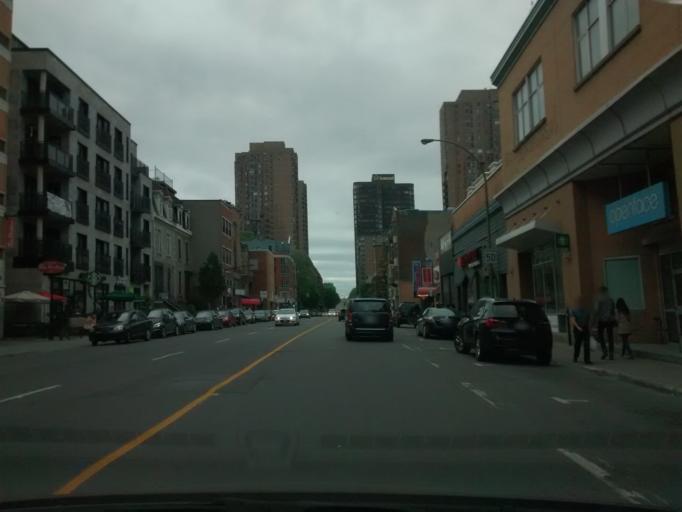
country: CA
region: Quebec
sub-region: Montreal
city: Montreal
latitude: 45.5088
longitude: -73.5720
